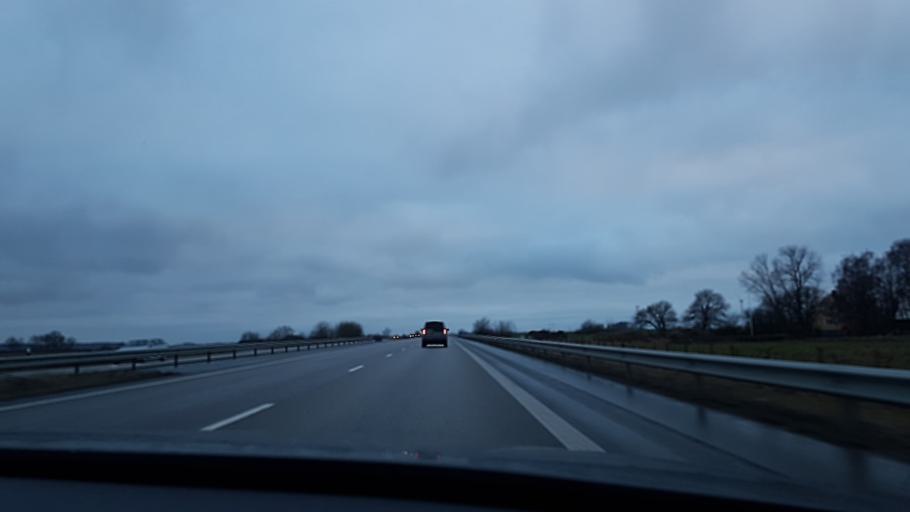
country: SE
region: Skane
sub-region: Astorps Kommun
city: Astorp
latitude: 56.1738
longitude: 12.9946
